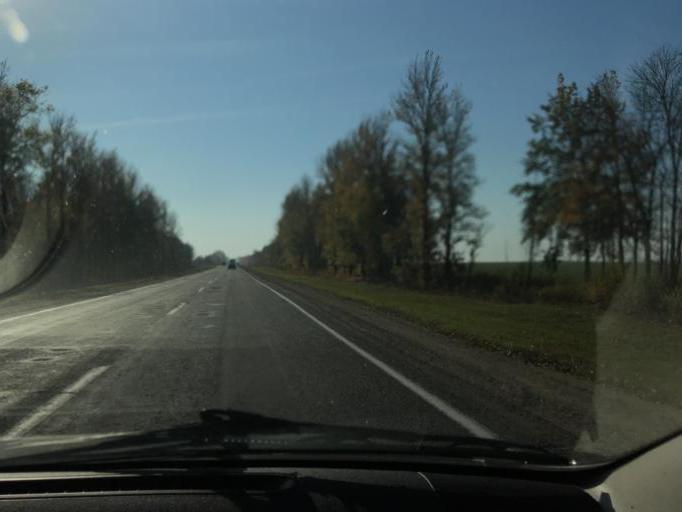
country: BY
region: Minsk
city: Salihorsk
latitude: 52.8964
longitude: 27.4742
